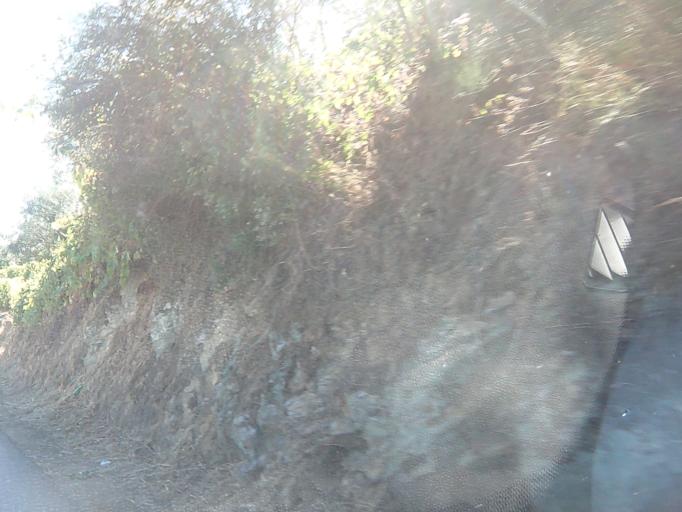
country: PT
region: Vila Real
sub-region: Santa Marta de Penaguiao
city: Santa Marta de Penaguiao
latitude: 41.2342
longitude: -7.7915
